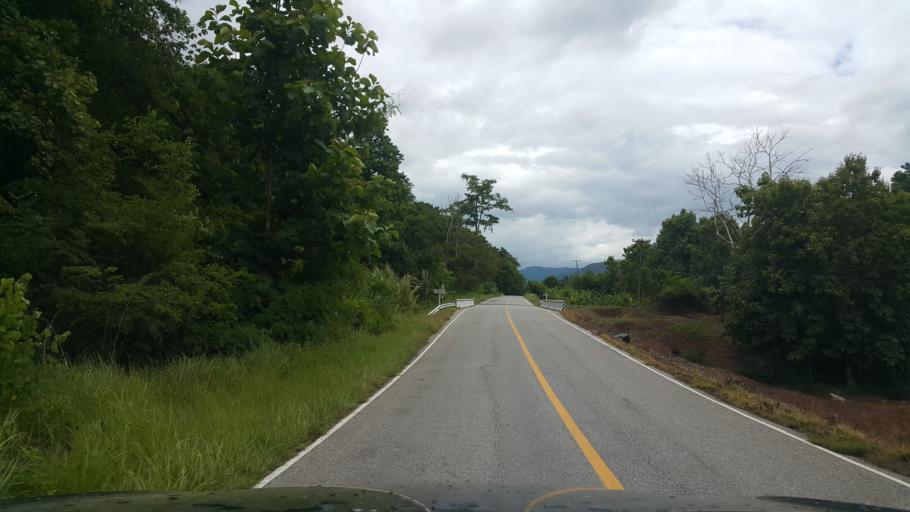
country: TH
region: Phitsanulok
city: Chat Trakan
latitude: 17.3403
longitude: 100.7115
